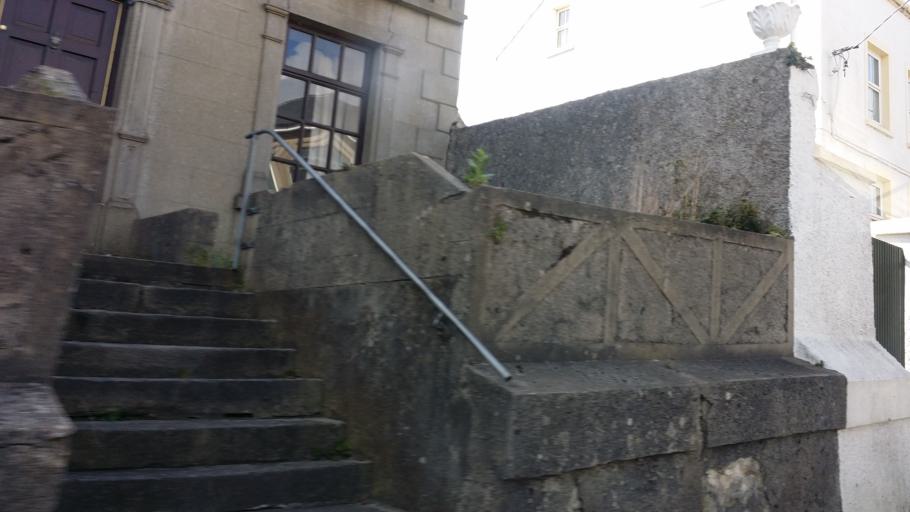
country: IE
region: Ulster
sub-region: County Donegal
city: Ballyshannon
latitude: 54.5030
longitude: -8.1921
